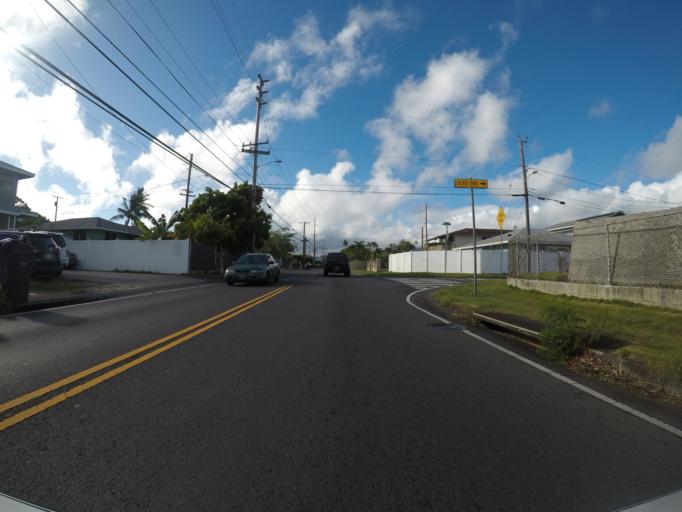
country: US
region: Hawaii
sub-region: Honolulu County
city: Kailua
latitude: 21.4063
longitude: -157.7515
